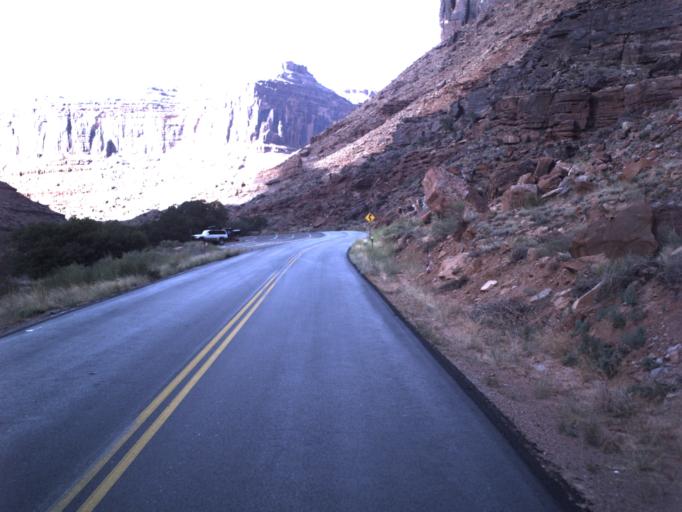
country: US
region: Utah
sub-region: Grand County
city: Moab
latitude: 38.6604
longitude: -109.5006
